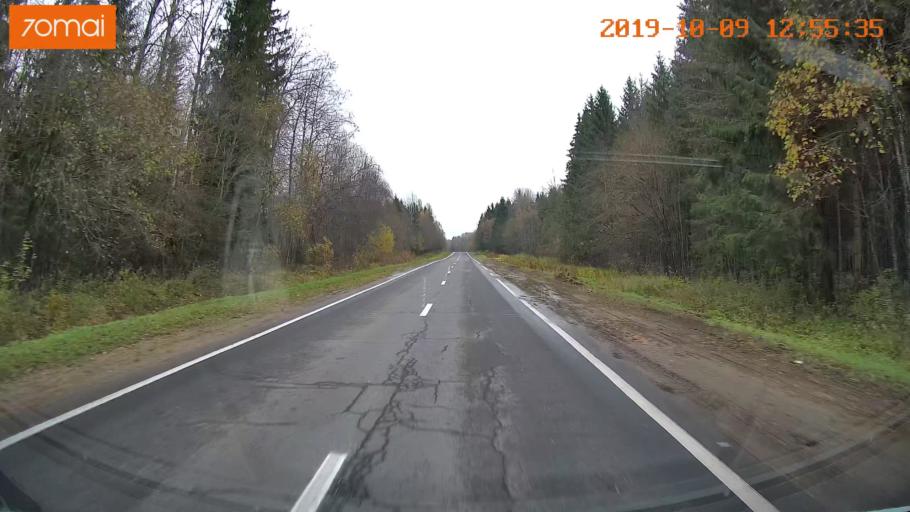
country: RU
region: Jaroslavl
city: Prechistoye
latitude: 58.3989
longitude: 40.3970
